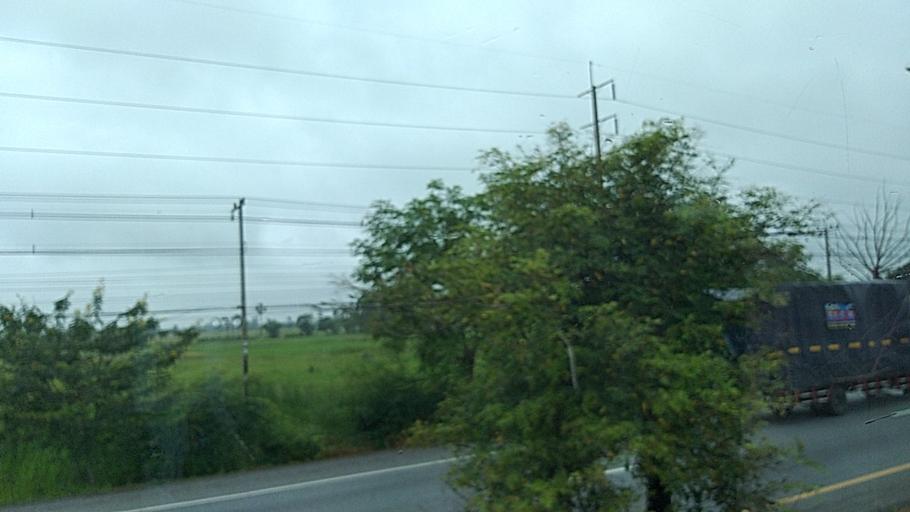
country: TH
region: Nakhon Ratchasima
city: Phimai
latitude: 15.2767
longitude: 102.4184
